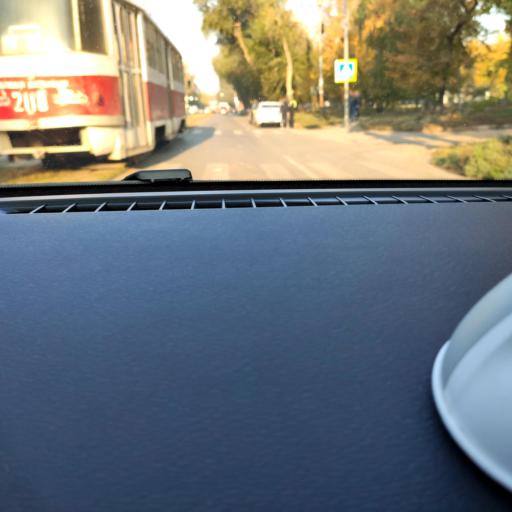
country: RU
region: Samara
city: Petra-Dubrava
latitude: 53.2392
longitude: 50.2828
